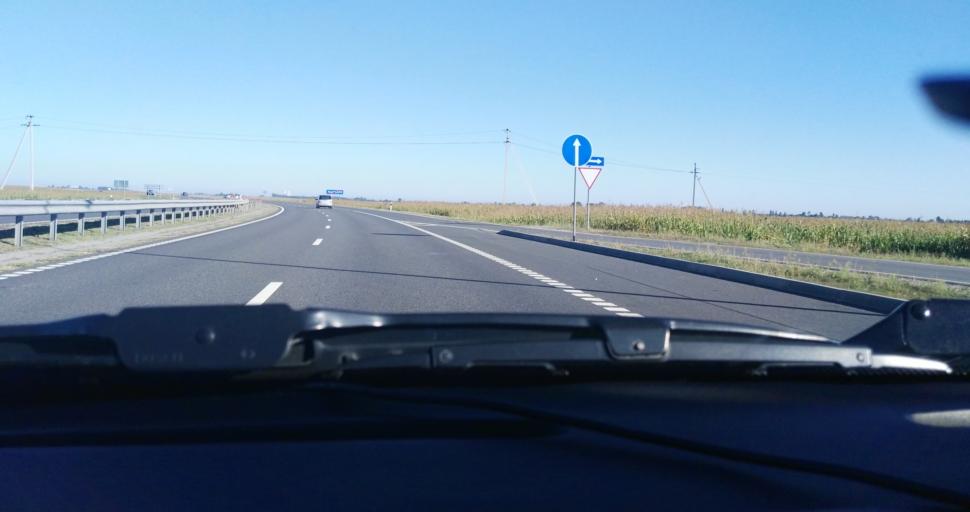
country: BY
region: Gomel
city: Buda-Kashalyova
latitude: 52.5200
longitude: 30.6266
